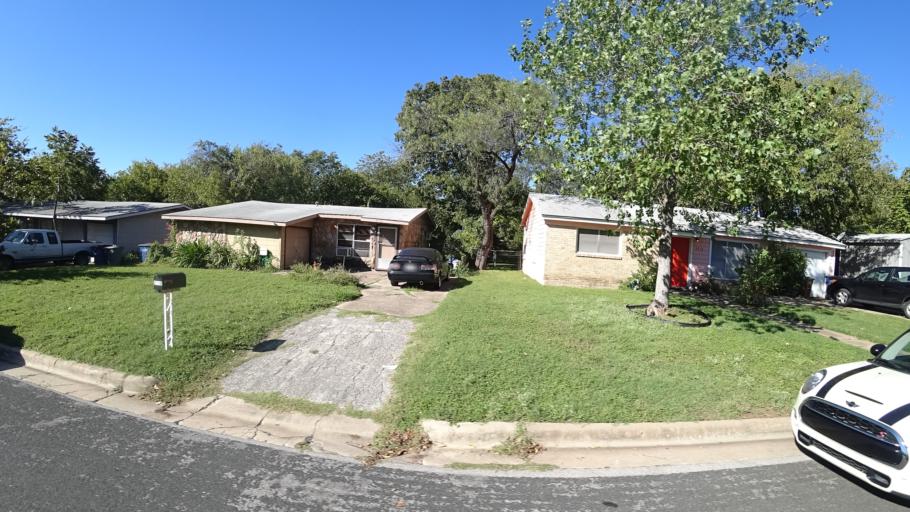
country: US
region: Texas
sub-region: Travis County
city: Austin
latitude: 30.2880
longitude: -97.7045
